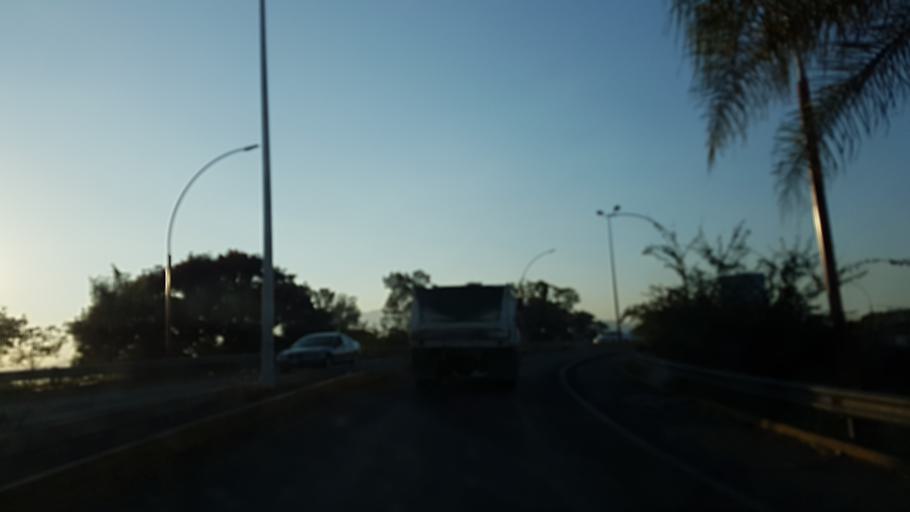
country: MX
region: Nayarit
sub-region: Tepic
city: La Corregidora
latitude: 21.4685
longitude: -104.8451
